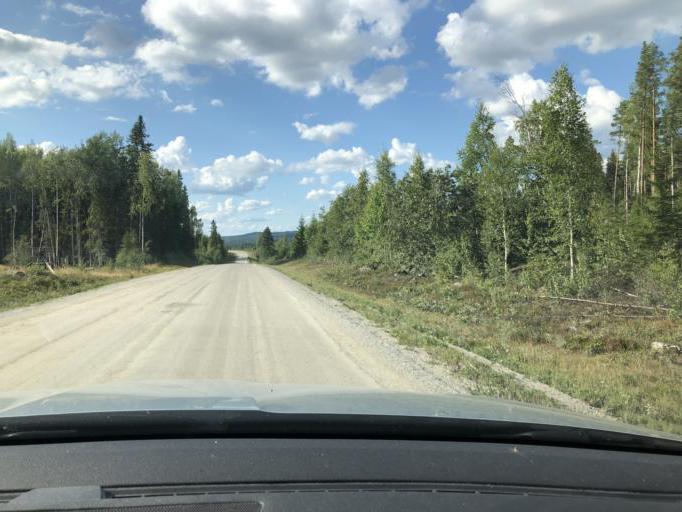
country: SE
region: Vaesternorrland
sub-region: Solleftea Kommun
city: Solleftea
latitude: 63.3161
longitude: 17.2447
